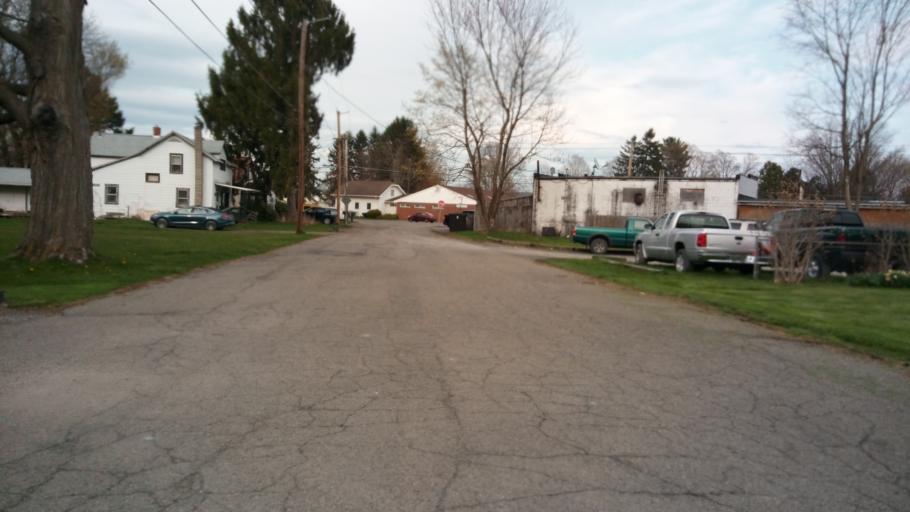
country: US
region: New York
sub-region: Chemung County
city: Southport
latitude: 42.0632
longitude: -76.8179
